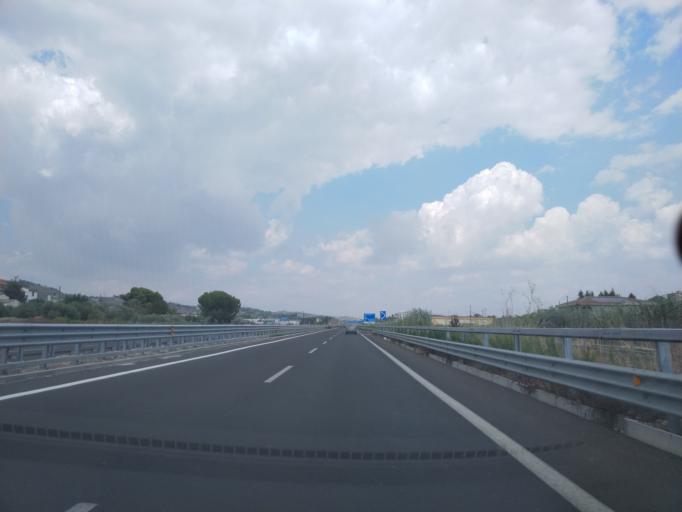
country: IT
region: Sicily
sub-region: Agrigento
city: Racalmuto
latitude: 37.3793
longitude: 13.7270
